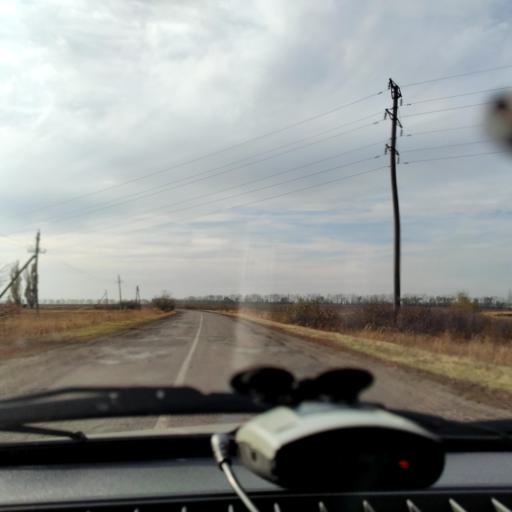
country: RU
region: Voronezj
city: Rossosh'
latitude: 51.2265
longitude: 38.7633
